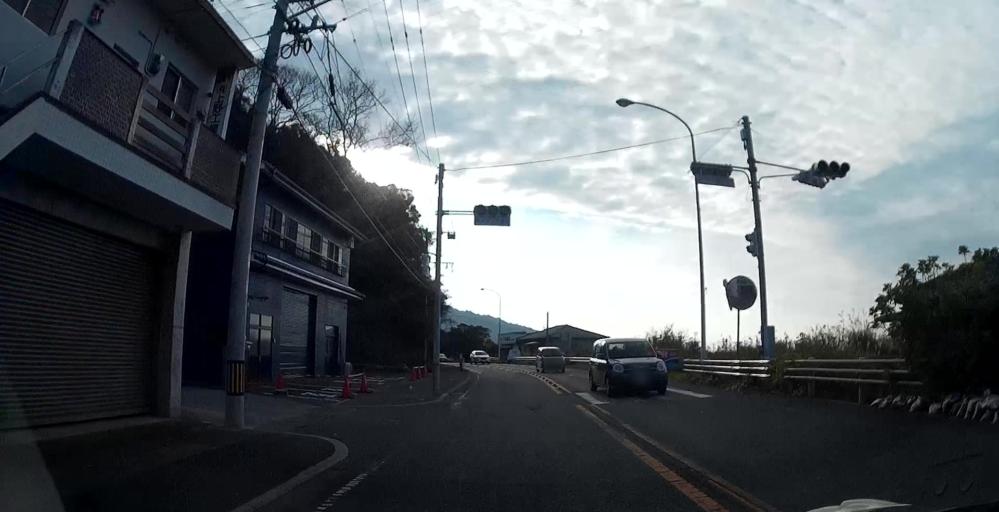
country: JP
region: Kumamoto
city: Matsubase
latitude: 32.6606
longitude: 130.5195
